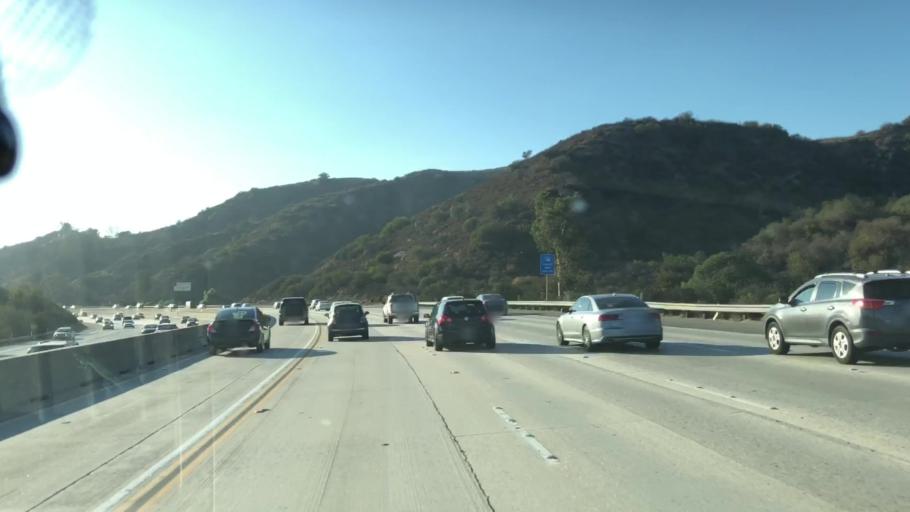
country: US
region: California
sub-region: Los Angeles County
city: La Canada Flintridge
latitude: 34.1474
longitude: -118.1986
